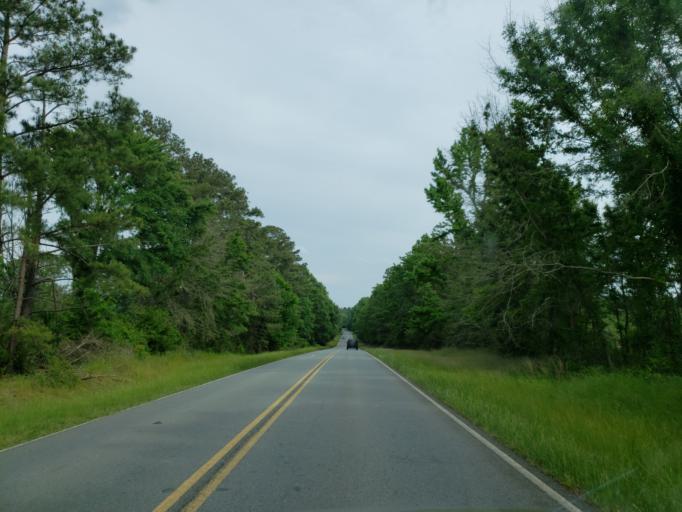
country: US
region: Georgia
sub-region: Macon County
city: Montezuma
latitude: 32.2127
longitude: -83.9275
